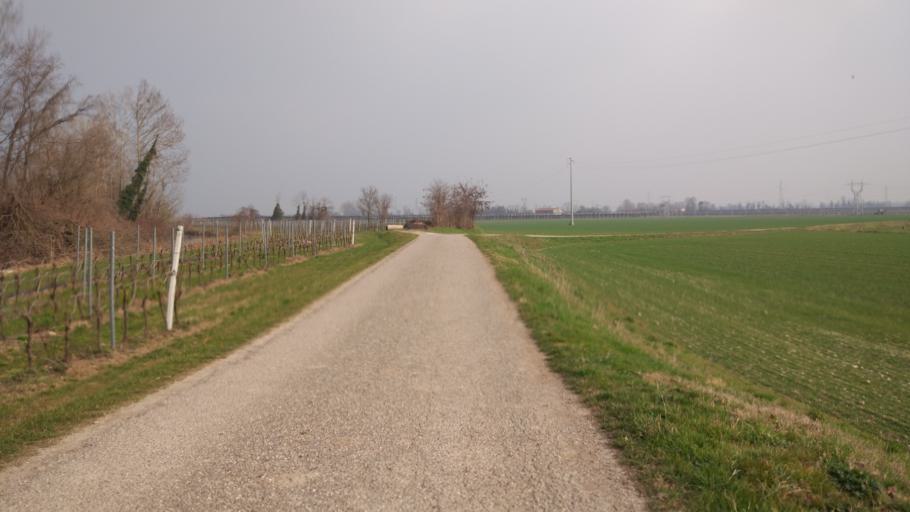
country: IT
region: Veneto
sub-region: Provincia di Verona
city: Caldierino-Rota
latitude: 45.3952
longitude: 11.1440
